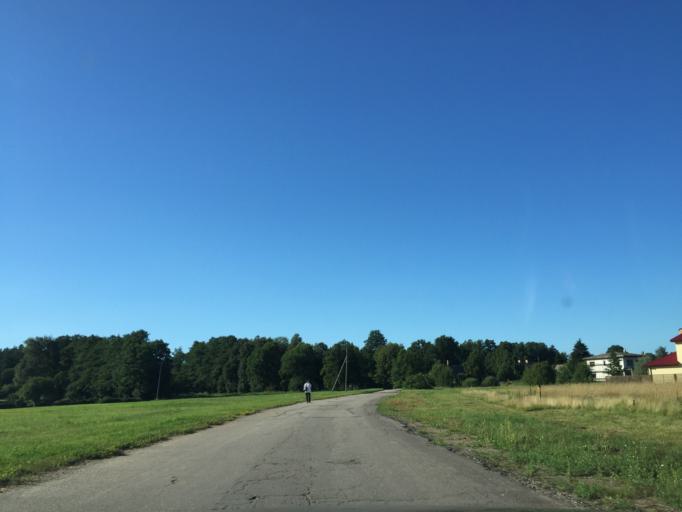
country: LV
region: Riga
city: Jaunciems
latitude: 57.0606
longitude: 24.1385
